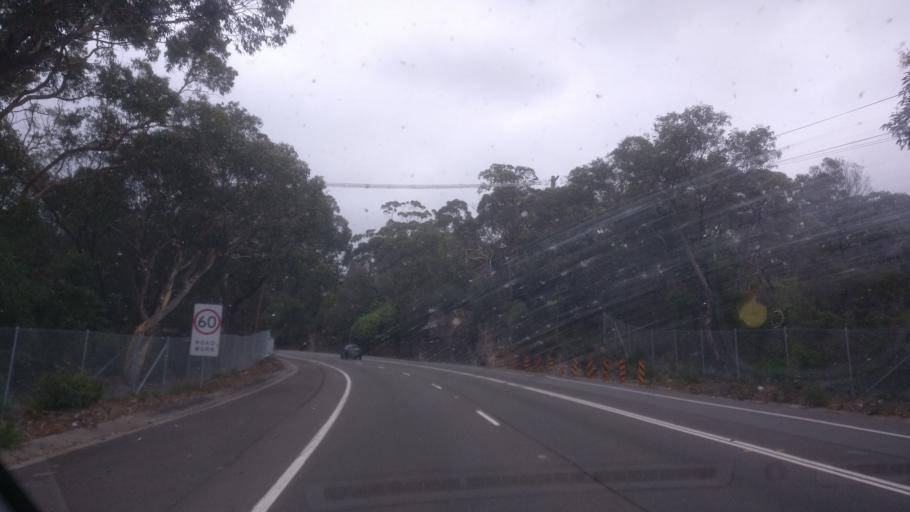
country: AU
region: New South Wales
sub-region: Warringah
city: Allambie Heights
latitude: -33.7455
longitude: 151.2348
